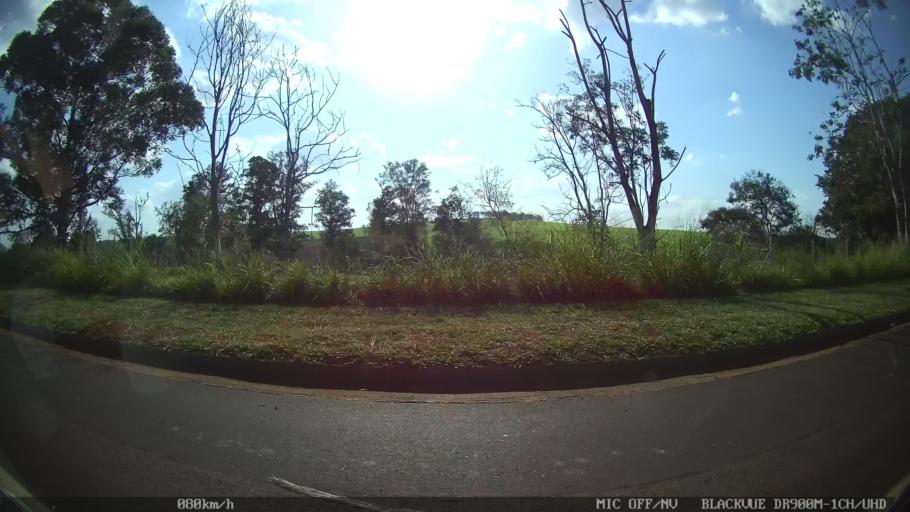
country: BR
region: Sao Paulo
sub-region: Ribeirao Preto
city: Ribeirao Preto
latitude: -21.1931
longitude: -47.8695
